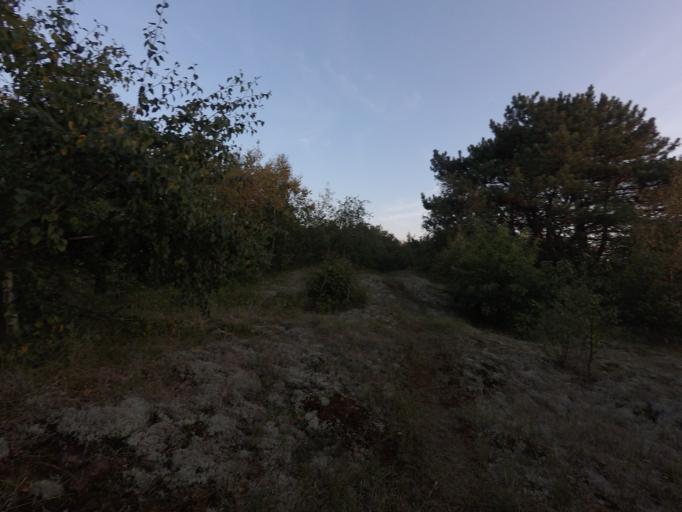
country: NL
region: Friesland
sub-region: Gemeente Schiermonnikoog
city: Schiermonnikoog
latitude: 53.4896
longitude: 6.1713
